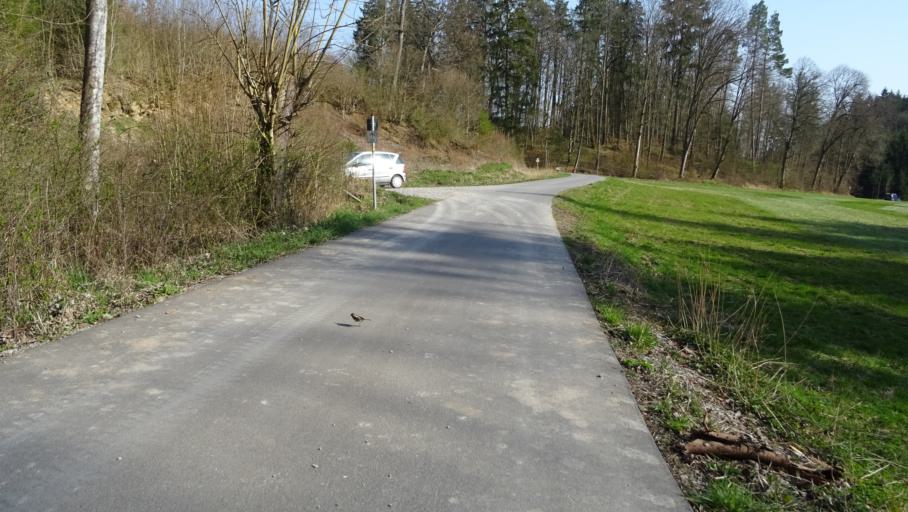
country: DE
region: Baden-Wuerttemberg
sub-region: Regierungsbezirk Stuttgart
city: Roigheim
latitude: 49.3864
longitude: 9.3419
